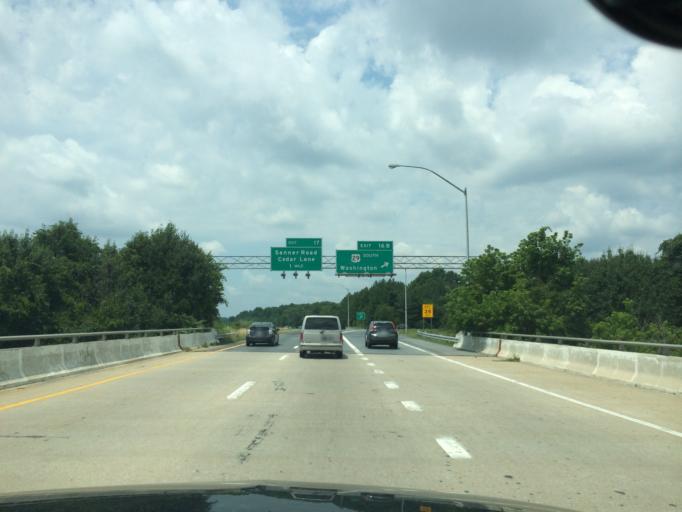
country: US
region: Maryland
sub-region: Howard County
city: Riverside
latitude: 39.1818
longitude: -76.8744
